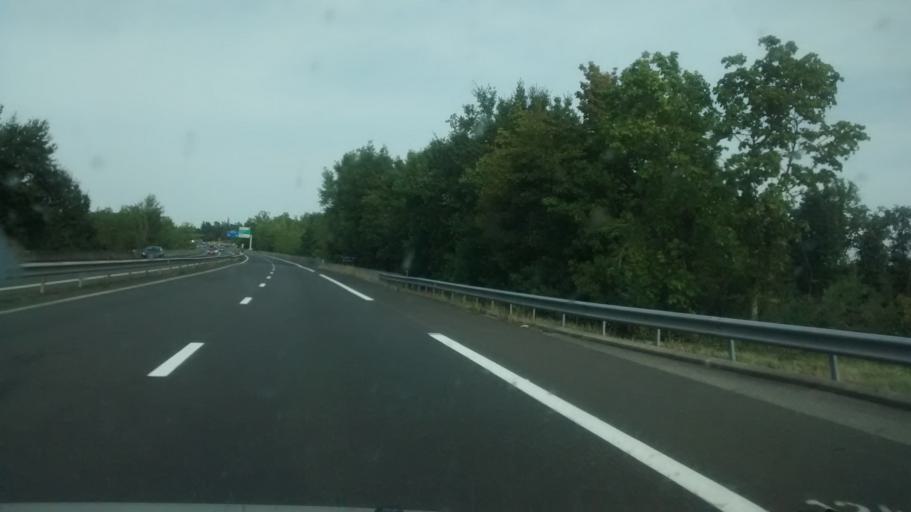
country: FR
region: Aquitaine
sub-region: Departement du Lot-et-Garonne
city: Boe
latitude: 44.1599
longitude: 0.6127
